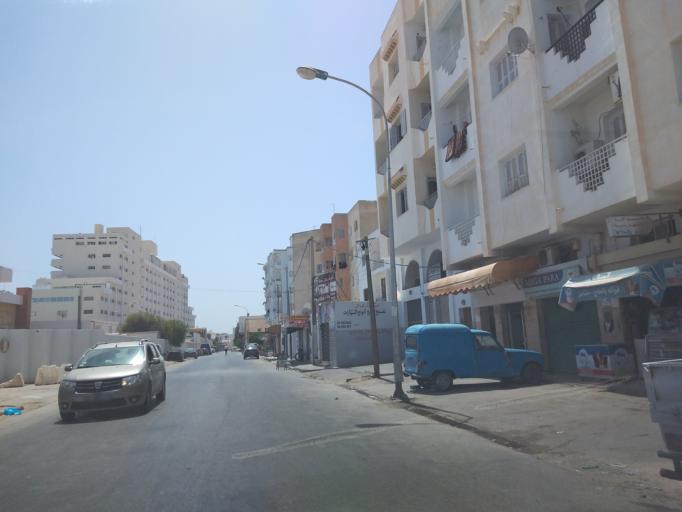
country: TN
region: Safaqis
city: Sfax
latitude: 34.7424
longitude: 10.7493
